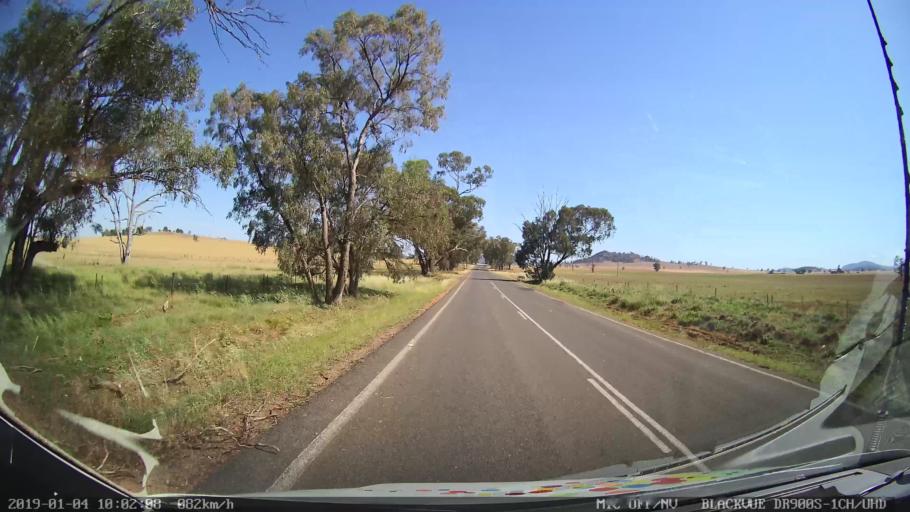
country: AU
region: New South Wales
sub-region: Cabonne
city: Canowindra
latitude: -33.4801
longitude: 148.3660
